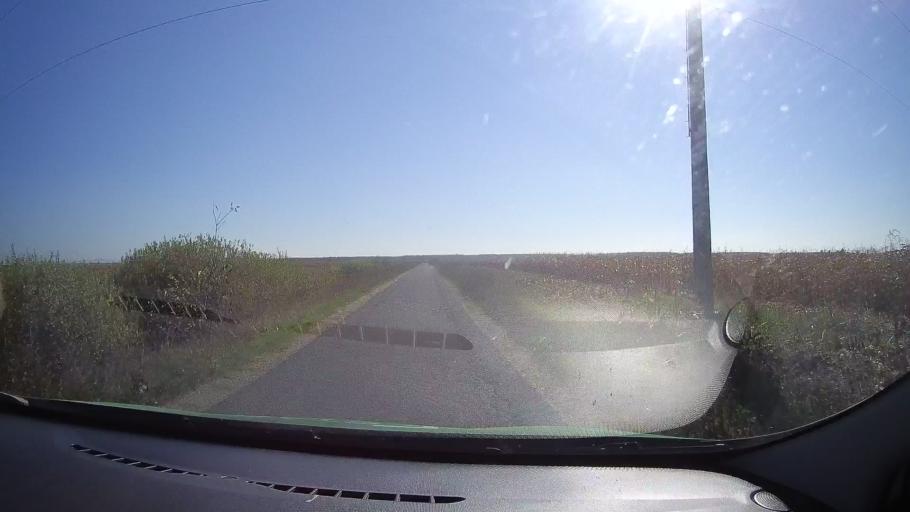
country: RO
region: Satu Mare
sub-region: Comuna Doba
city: Doba
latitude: 47.7354
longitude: 22.7211
